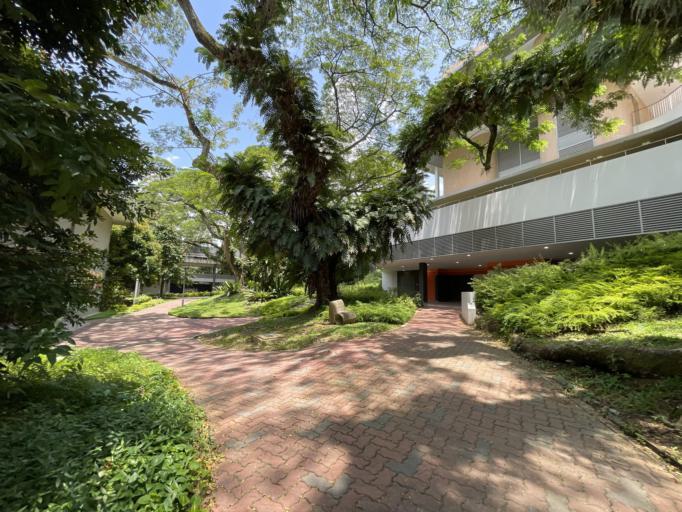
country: SG
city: Singapore
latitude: 1.2975
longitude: 103.7714
